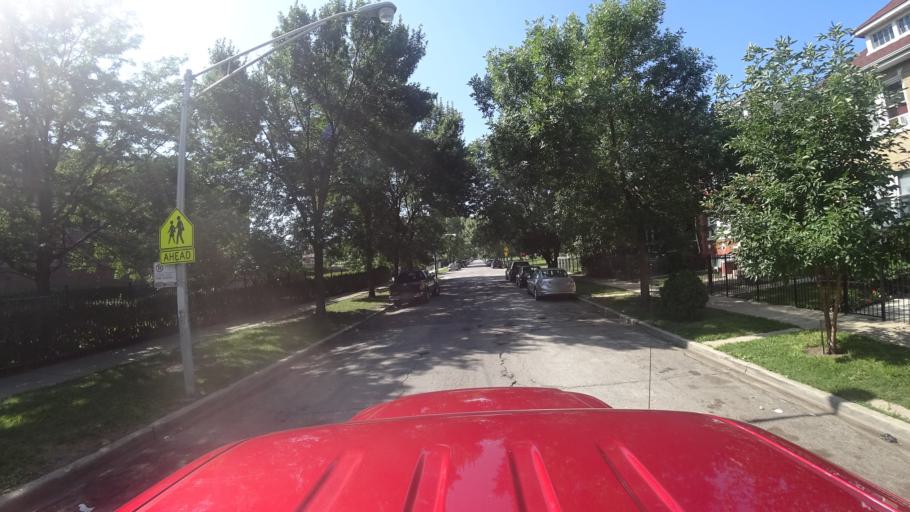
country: US
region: Illinois
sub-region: Cook County
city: Chicago
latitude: 41.7925
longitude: -87.6889
